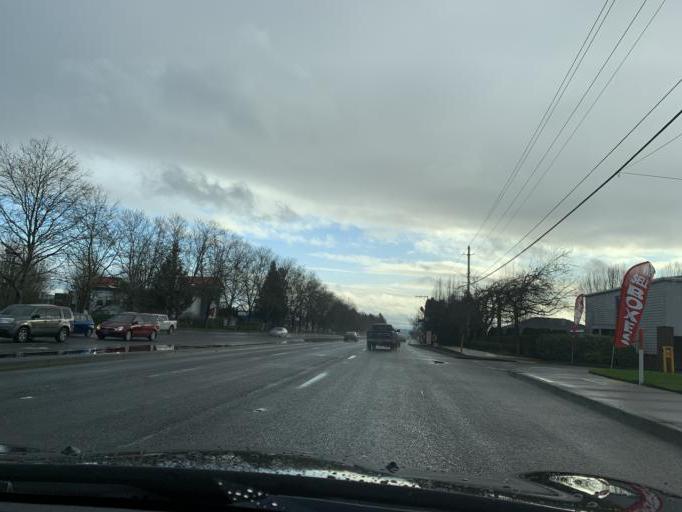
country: US
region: Washington
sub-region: Clark County
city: Mill Plain
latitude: 45.6037
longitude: -122.5040
